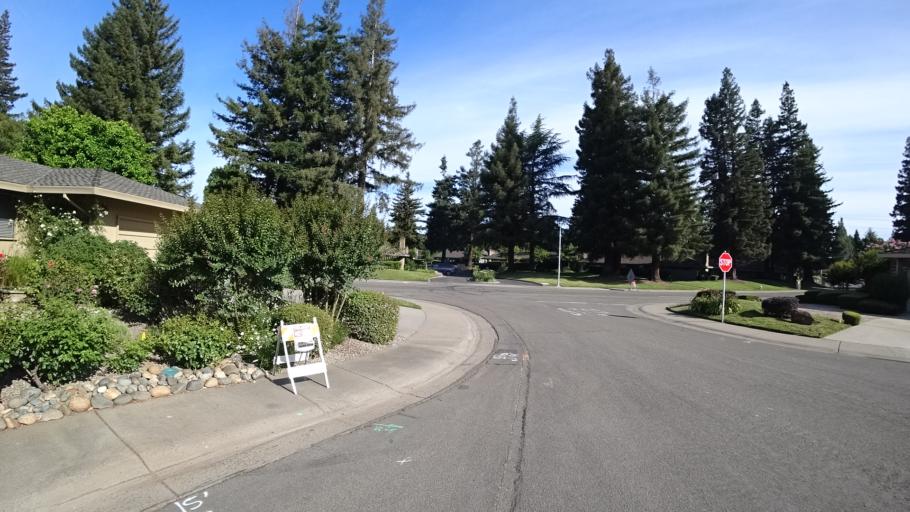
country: US
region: California
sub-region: Sacramento County
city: Rosemont
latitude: 38.5677
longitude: -121.4037
